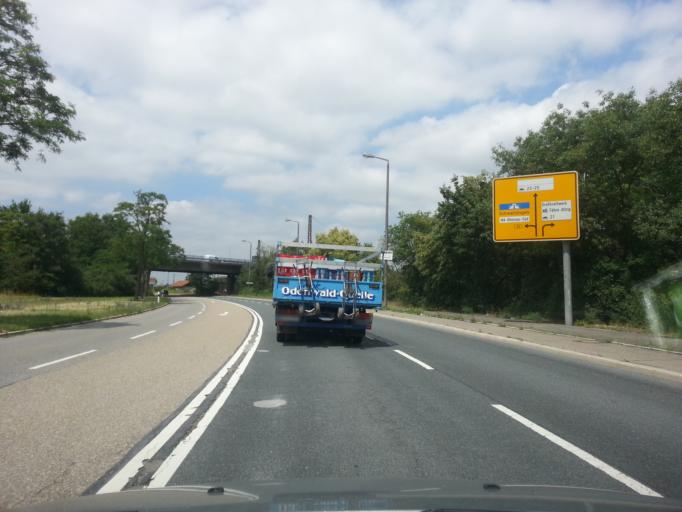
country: DE
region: Baden-Wuerttemberg
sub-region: Karlsruhe Region
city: Bruhl
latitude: 49.4200
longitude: 8.5389
